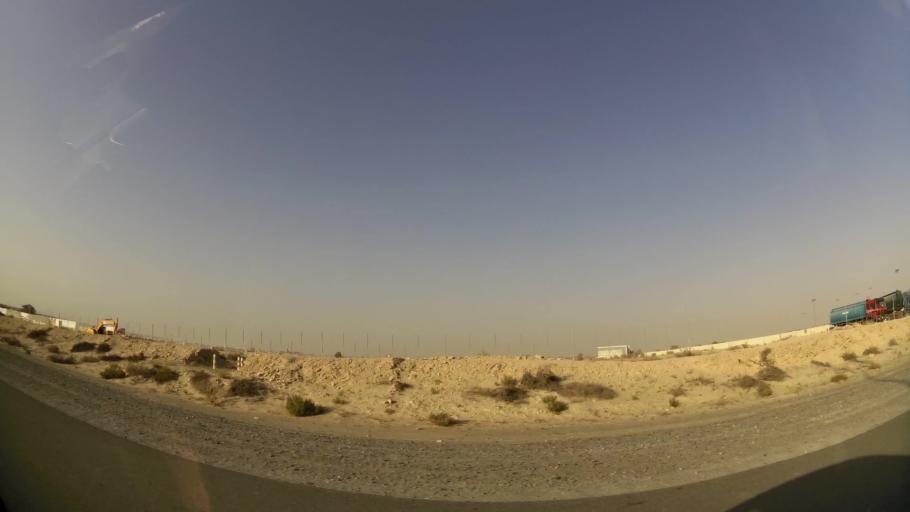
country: AE
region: Dubai
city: Dubai
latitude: 25.0867
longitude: 55.2483
